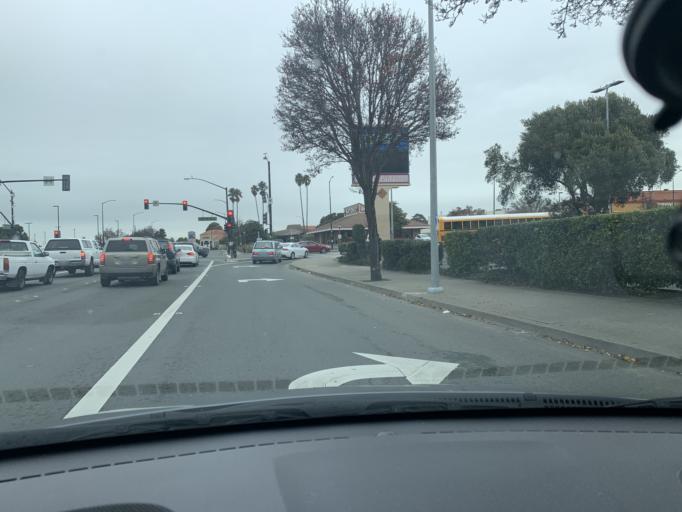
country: US
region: California
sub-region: Contra Costa County
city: Rollingwood
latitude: 37.9528
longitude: -122.3333
